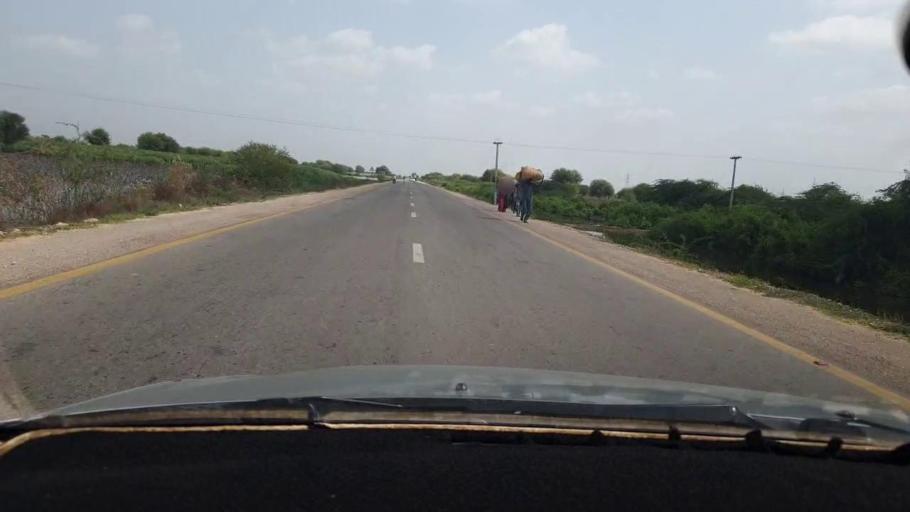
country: PK
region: Sindh
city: Digri
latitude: 25.1085
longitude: 69.1638
